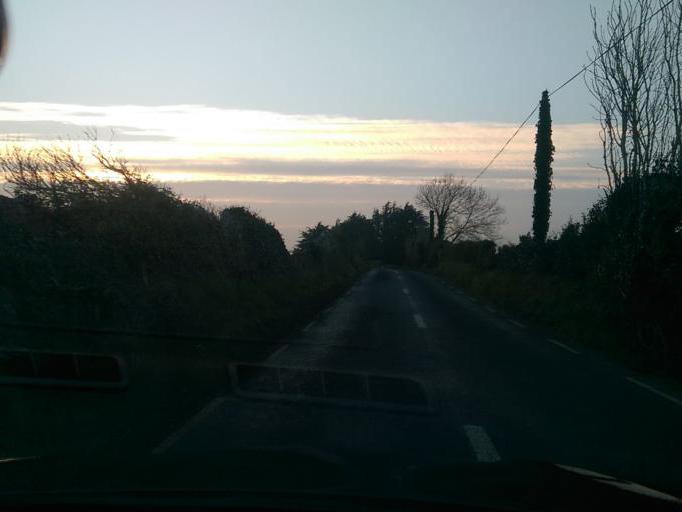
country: IE
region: Connaught
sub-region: County Galway
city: Loughrea
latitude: 53.2302
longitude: -8.6431
